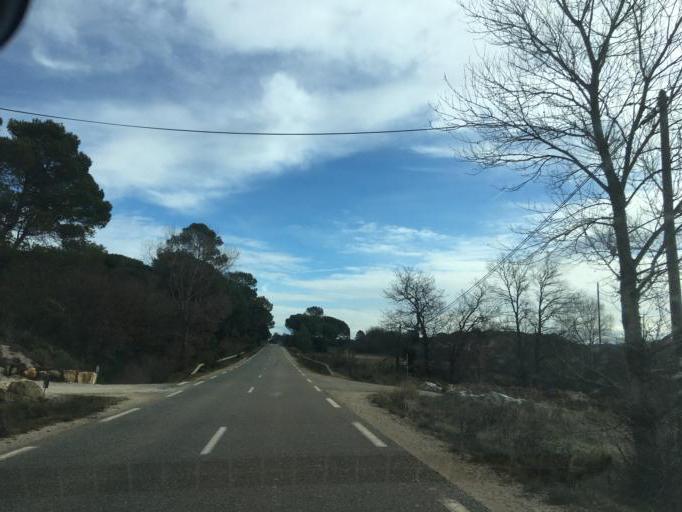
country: FR
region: Provence-Alpes-Cote d'Azur
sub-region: Departement du Var
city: La Celle
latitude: 43.4454
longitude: 6.0111
